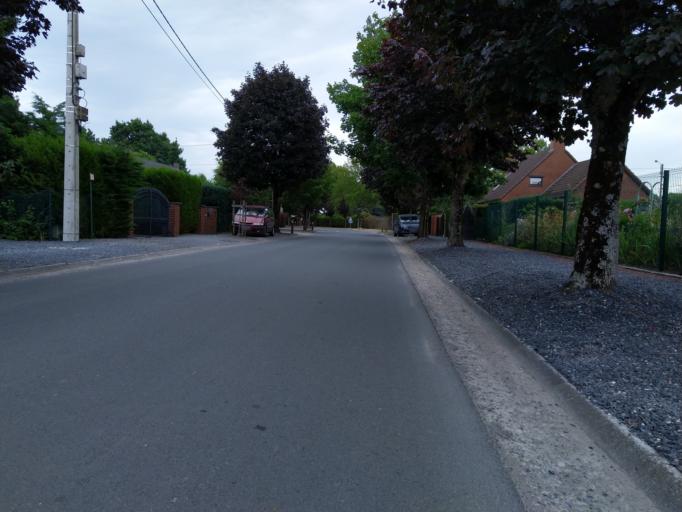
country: BE
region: Wallonia
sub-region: Province du Hainaut
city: Mons
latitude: 50.4640
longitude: 3.9852
